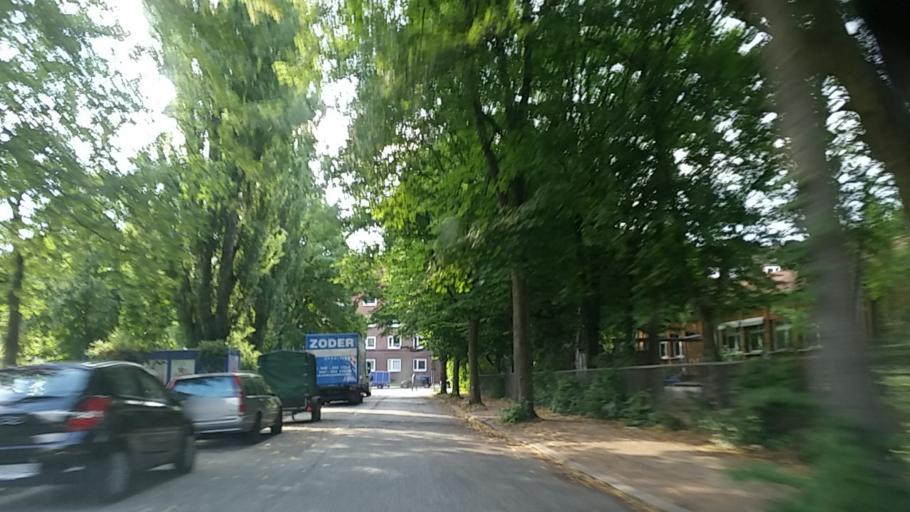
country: DE
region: Hamburg
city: Marienthal
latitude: 53.5517
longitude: 10.0817
